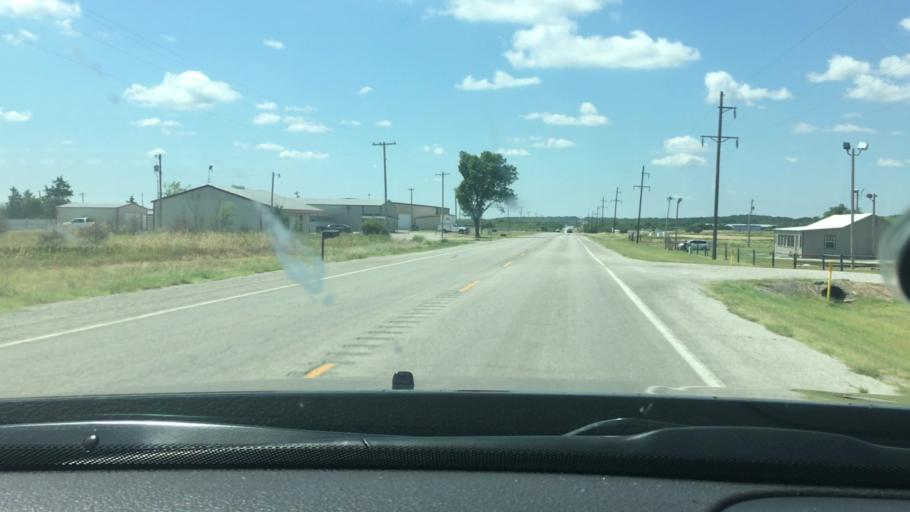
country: US
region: Oklahoma
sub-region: Carter County
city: Ardmore
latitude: 34.0875
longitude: -97.1429
